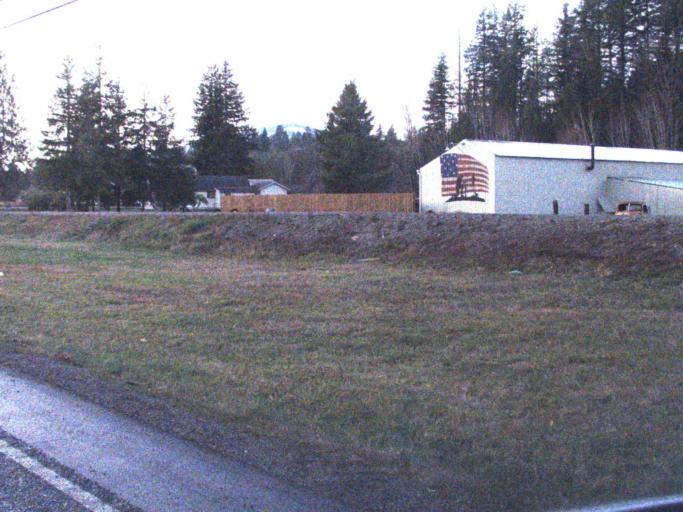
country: US
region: Washington
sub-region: Skagit County
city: Sedro-Woolley
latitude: 48.5251
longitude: -121.9410
